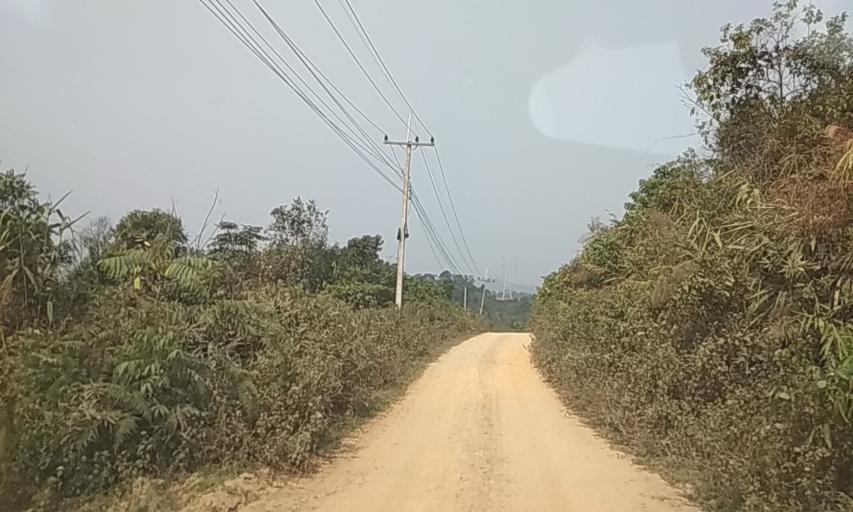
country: TH
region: Nan
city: Chaloem Phra Kiat
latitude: 20.0085
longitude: 101.1200
